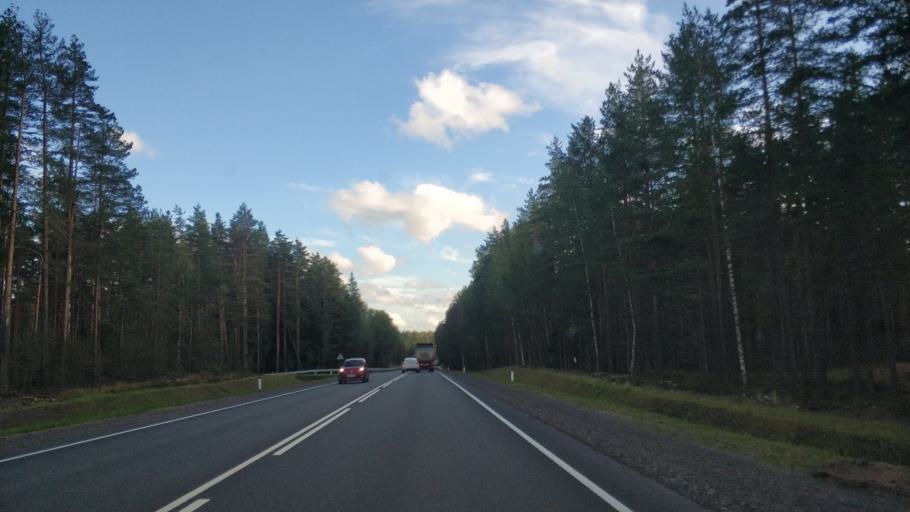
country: RU
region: Leningrad
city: Priozersk
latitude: 60.8798
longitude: 30.1609
